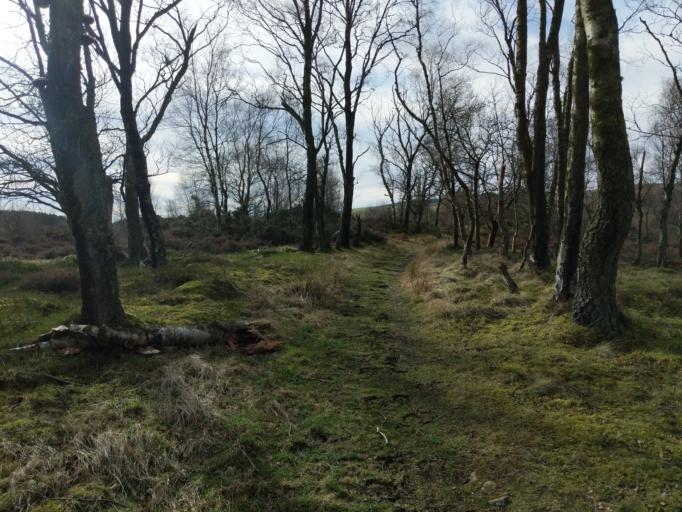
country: GB
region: Scotland
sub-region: The Scottish Borders
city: Peebles
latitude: 55.7119
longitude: -3.2282
